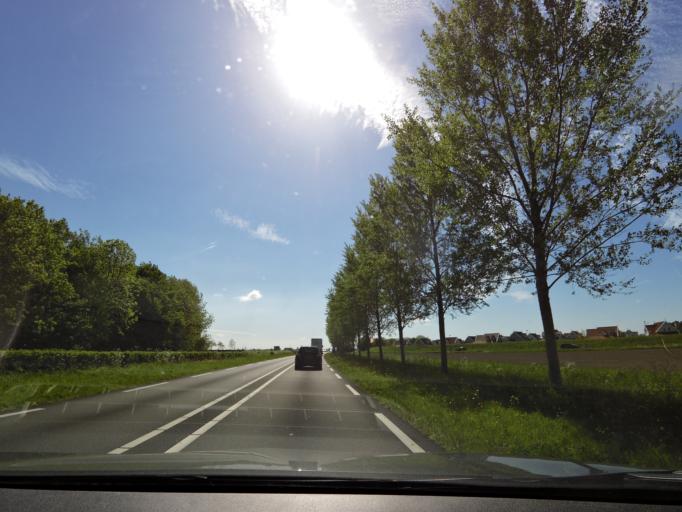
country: NL
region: Zeeland
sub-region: Schouwen-Duiveland
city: Bruinisse
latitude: 51.6626
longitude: 4.0865
